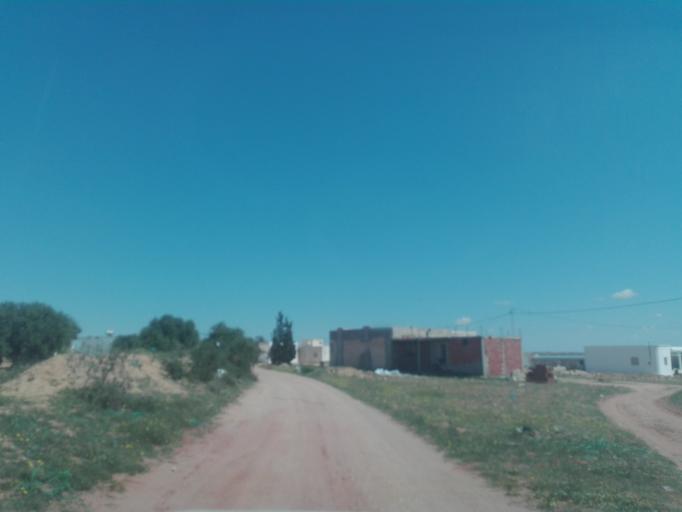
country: TN
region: Safaqis
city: Sfax
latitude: 34.7331
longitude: 10.4336
